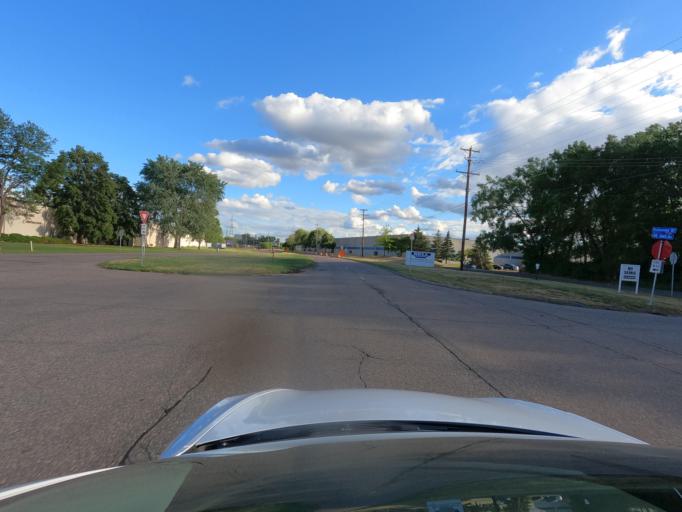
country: US
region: Minnesota
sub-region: Anoka County
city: Columbia Heights
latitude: 45.0324
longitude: -93.2767
